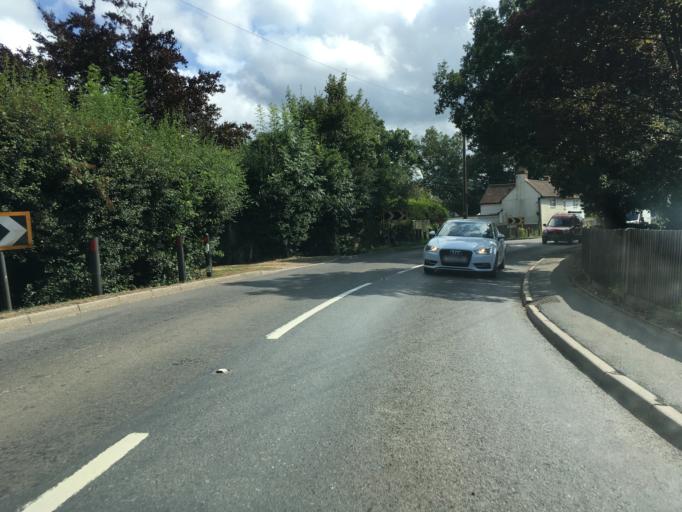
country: GB
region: England
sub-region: Kent
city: Headcorn
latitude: 51.1244
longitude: 0.6485
